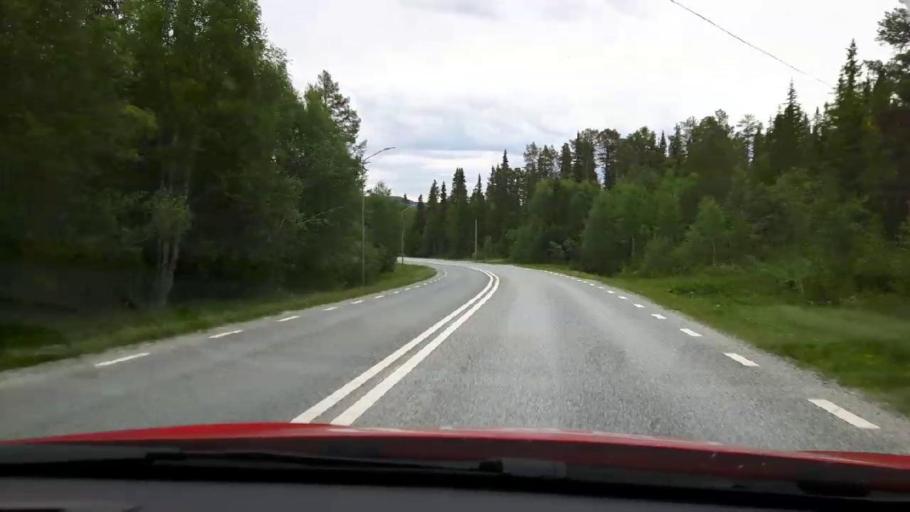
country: NO
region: Hedmark
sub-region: Engerdal
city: Engerdal
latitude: 62.5465
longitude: 12.4803
